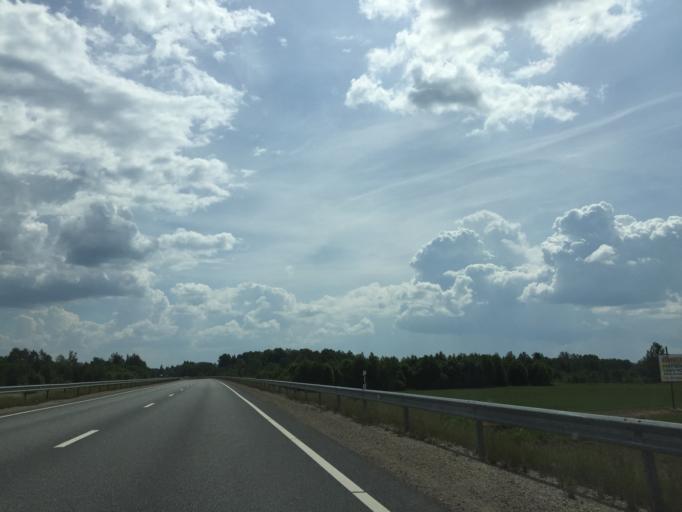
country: LV
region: Skriveri
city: Skriveri
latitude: 56.7440
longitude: 25.1286
